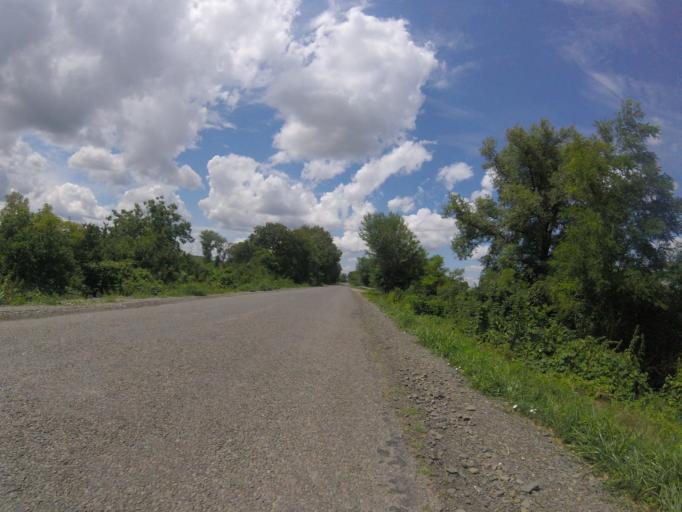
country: HU
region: Tolna
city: Ocseny
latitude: 46.3370
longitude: 18.7872
